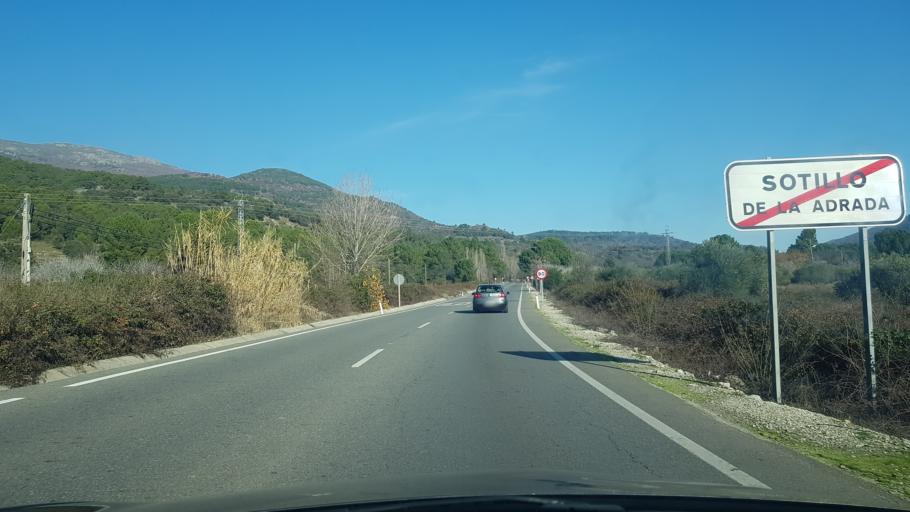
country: ES
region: Castille and Leon
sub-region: Provincia de Avila
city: Sotillo de la Adrada
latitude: 40.2978
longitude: -4.5728
